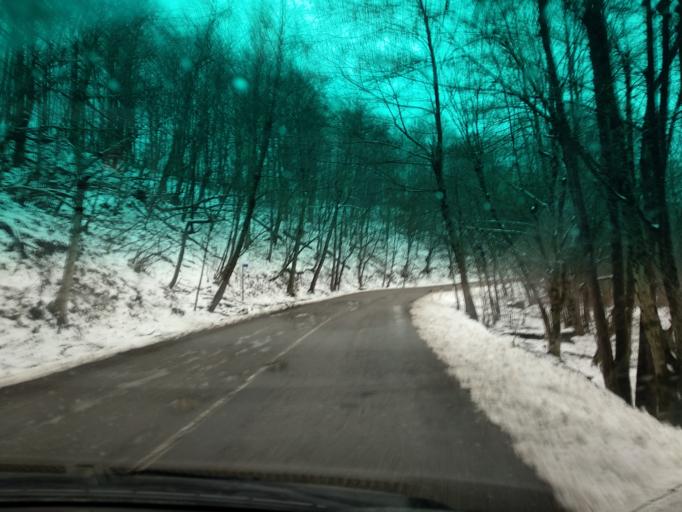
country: RU
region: Krasnodarskiy
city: Khadyzhensk
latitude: 44.2089
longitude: 39.4229
